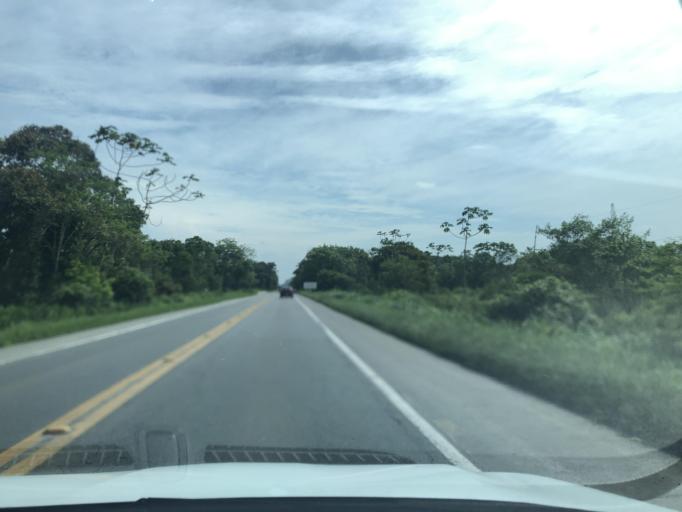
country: BR
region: Santa Catarina
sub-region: Sao Francisco Do Sul
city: Sao Francisco do Sul
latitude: -26.3255
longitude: -48.6495
